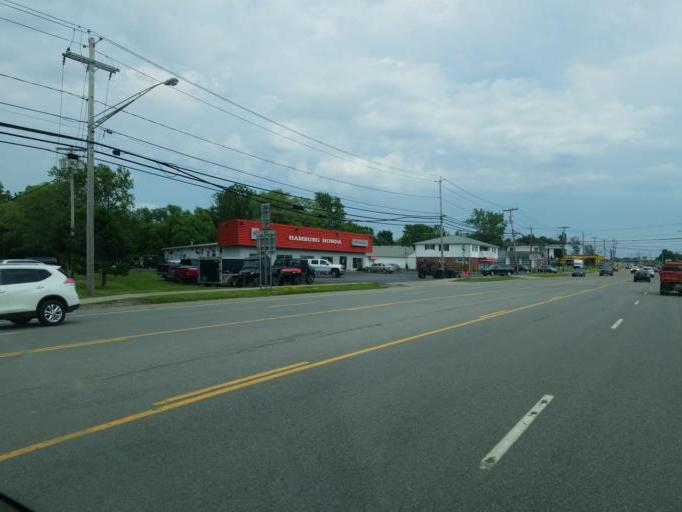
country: US
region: New York
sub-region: Erie County
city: Hamburg
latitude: 42.7482
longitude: -78.8535
